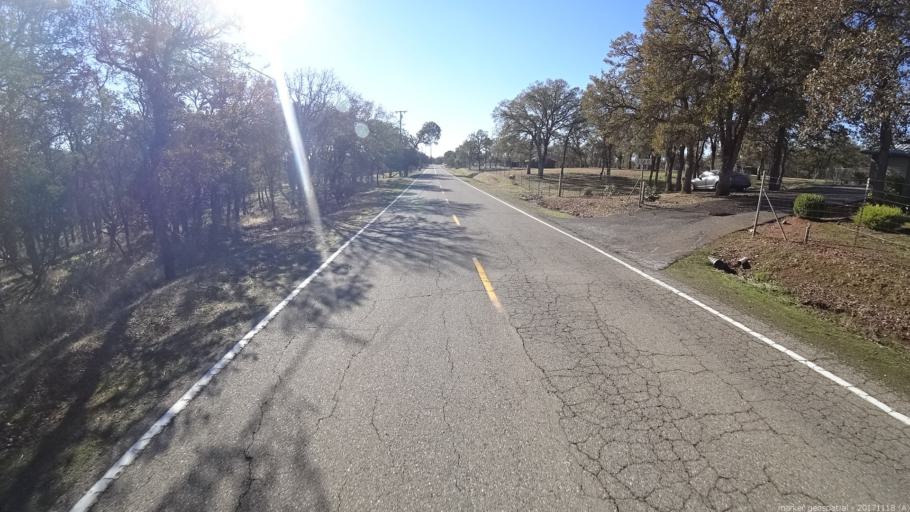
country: US
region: California
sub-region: Shasta County
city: Cottonwood
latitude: 40.3964
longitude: -122.3144
